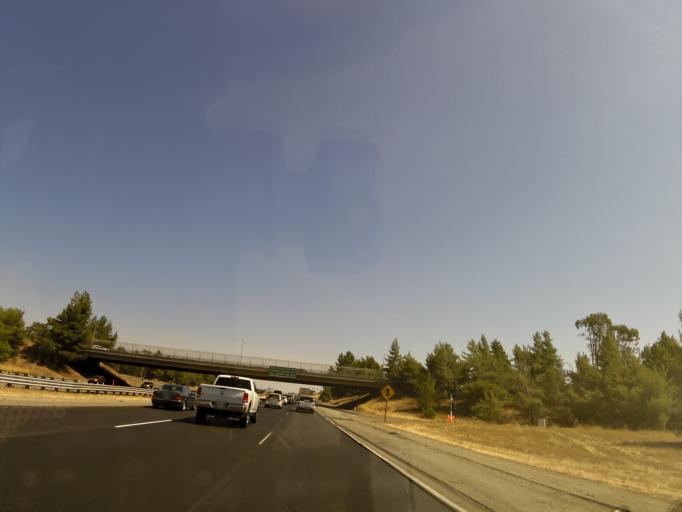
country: US
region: California
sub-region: Santa Clara County
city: Morgan Hill
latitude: 37.1539
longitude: -121.6536
